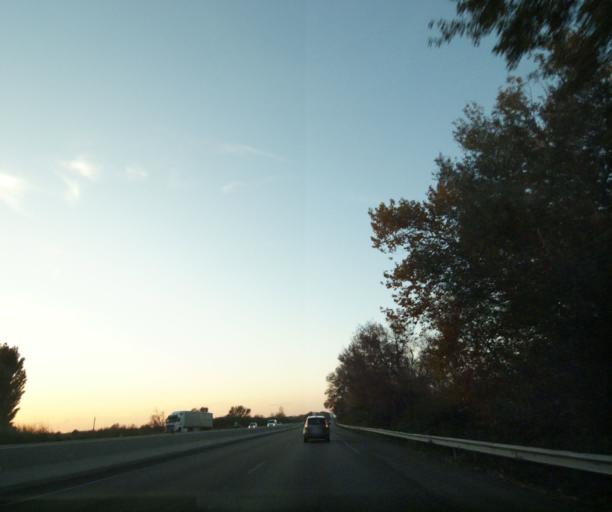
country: FR
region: Provence-Alpes-Cote d'Azur
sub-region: Departement des Bouches-du-Rhone
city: Saint-Martin-de-Crau
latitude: 43.6324
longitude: 4.7438
